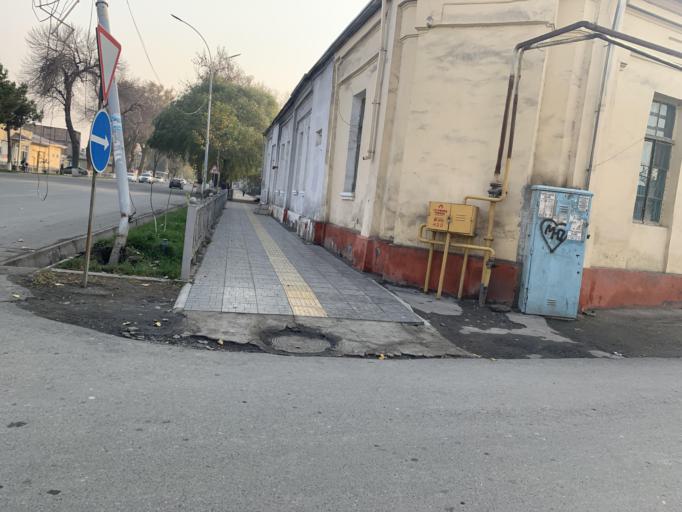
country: UZ
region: Fergana
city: Qo`qon
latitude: 40.5336
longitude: 70.9376
